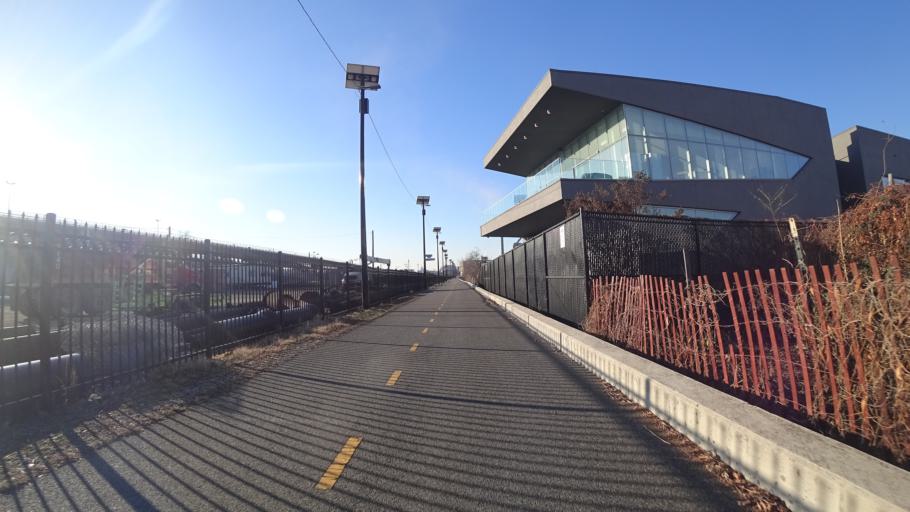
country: US
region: Maryland
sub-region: Prince George's County
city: Mount Rainier
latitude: 38.9184
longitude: -76.9984
